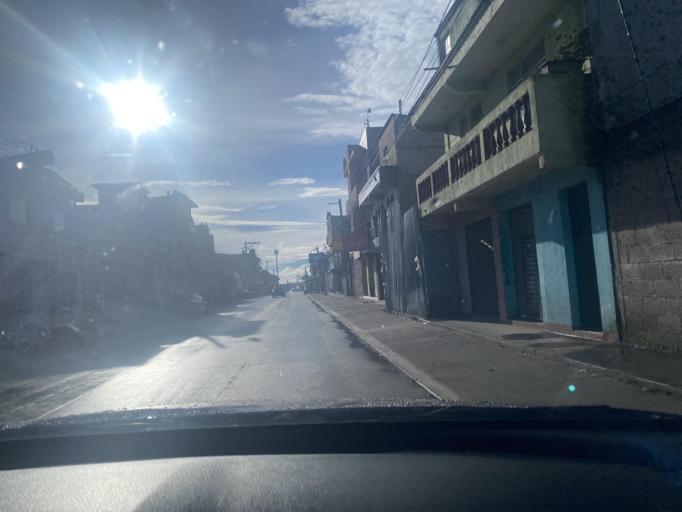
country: GT
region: Quetzaltenango
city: Olintepeque
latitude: 14.8656
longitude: -91.5150
